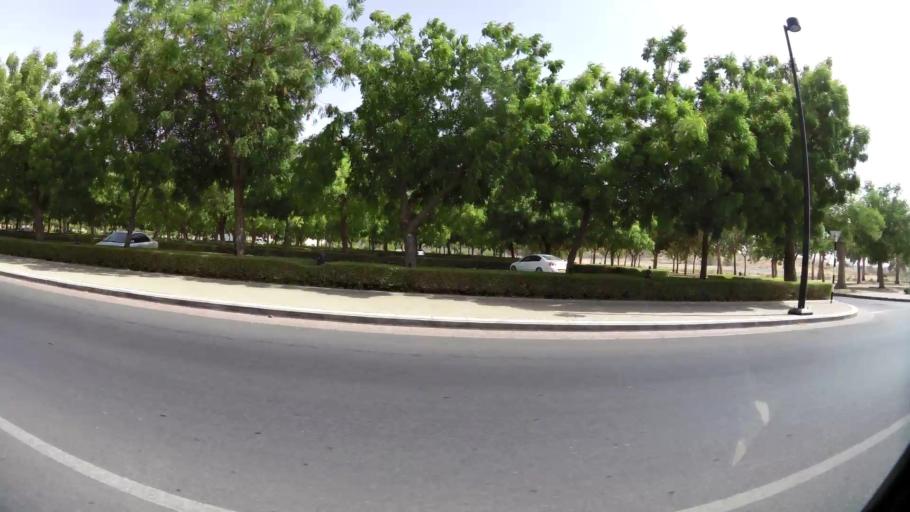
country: OM
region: Muhafazat Masqat
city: Bawshar
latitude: 23.5819
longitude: 58.3880
